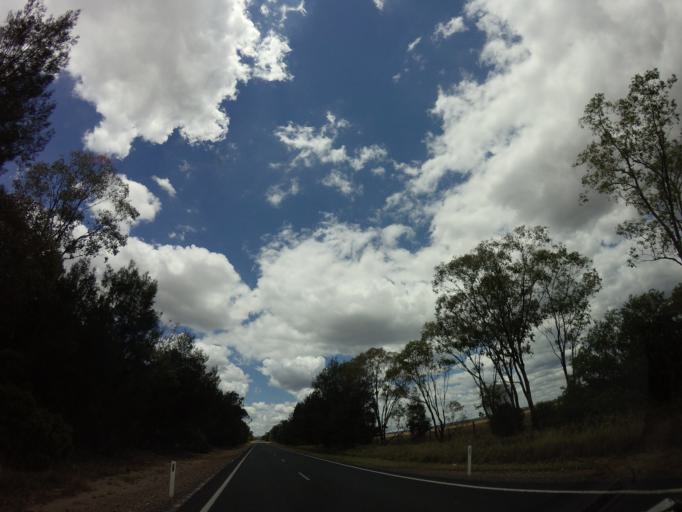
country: AU
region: Queensland
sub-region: Goondiwindi
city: Goondiwindi
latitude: -28.0074
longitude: 150.8837
